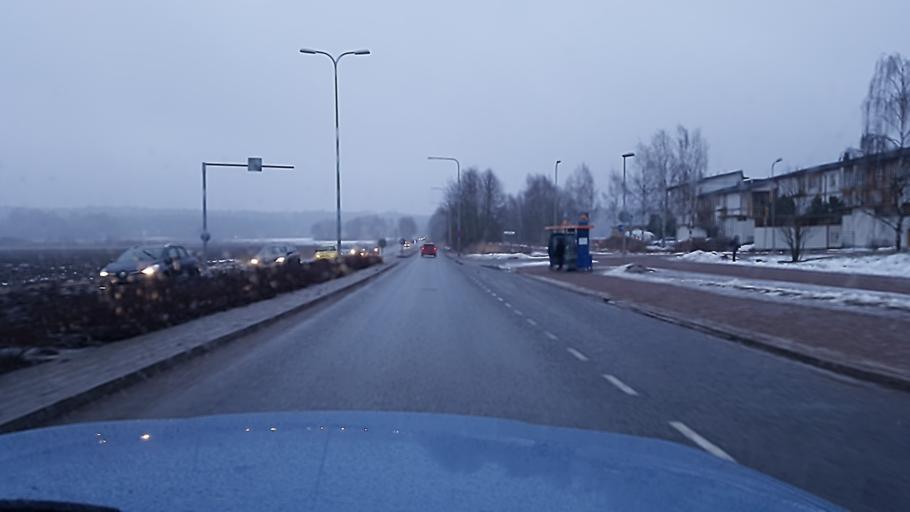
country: FI
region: Uusimaa
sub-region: Helsinki
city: Vantaa
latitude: 60.2239
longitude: 25.0215
